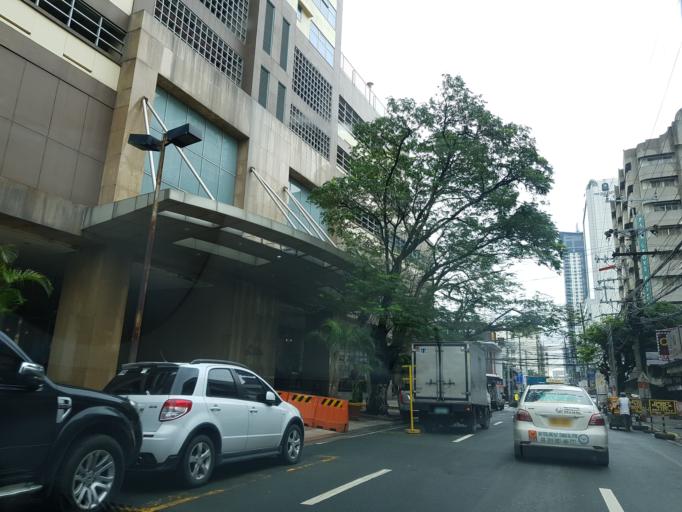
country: PH
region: Metro Manila
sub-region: City of Manila
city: Port Area
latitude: 14.5748
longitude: 120.9835
